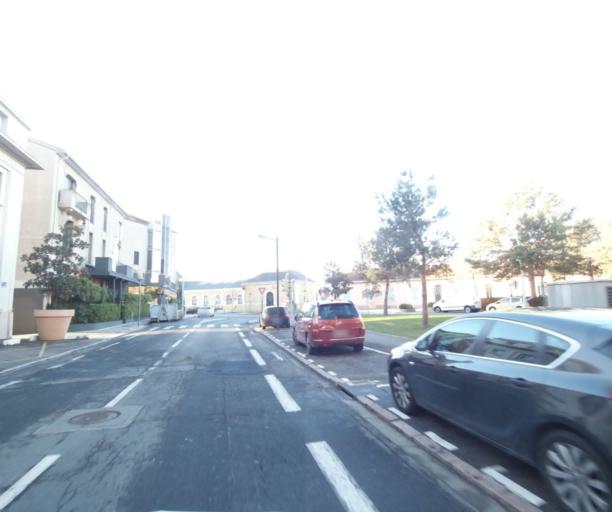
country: FR
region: Rhone-Alpes
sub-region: Departement de la Loire
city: Roanne
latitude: 46.0404
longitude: 4.0640
